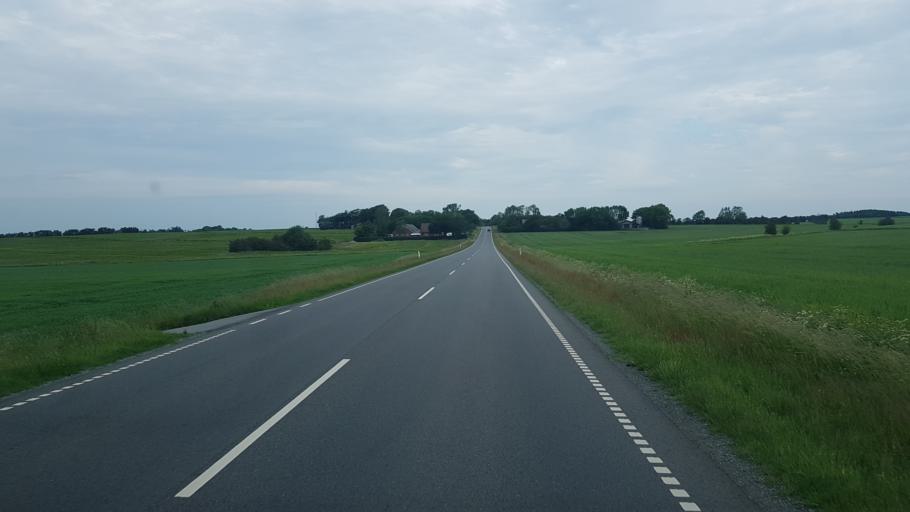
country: DK
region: South Denmark
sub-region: Vejen Kommune
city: Rodding
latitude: 55.4137
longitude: 9.0282
